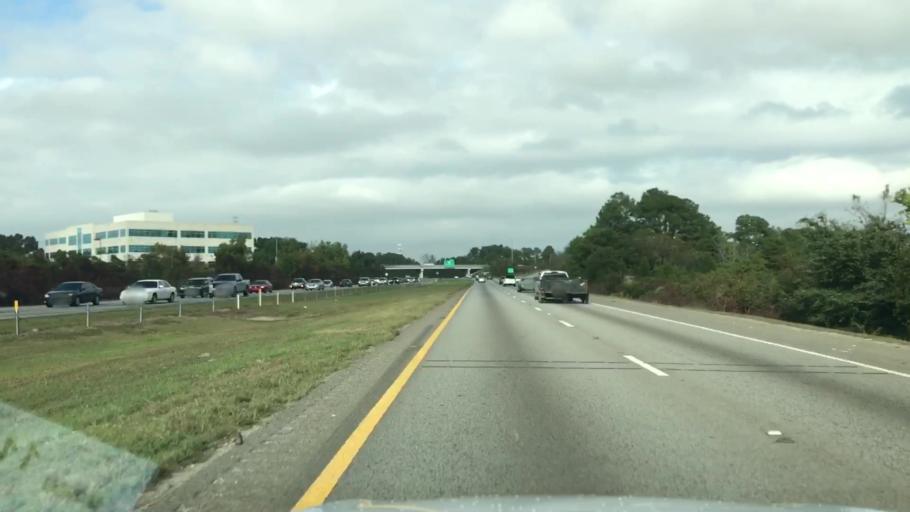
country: US
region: South Carolina
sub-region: Charleston County
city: North Charleston
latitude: 32.8385
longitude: -80.0216
